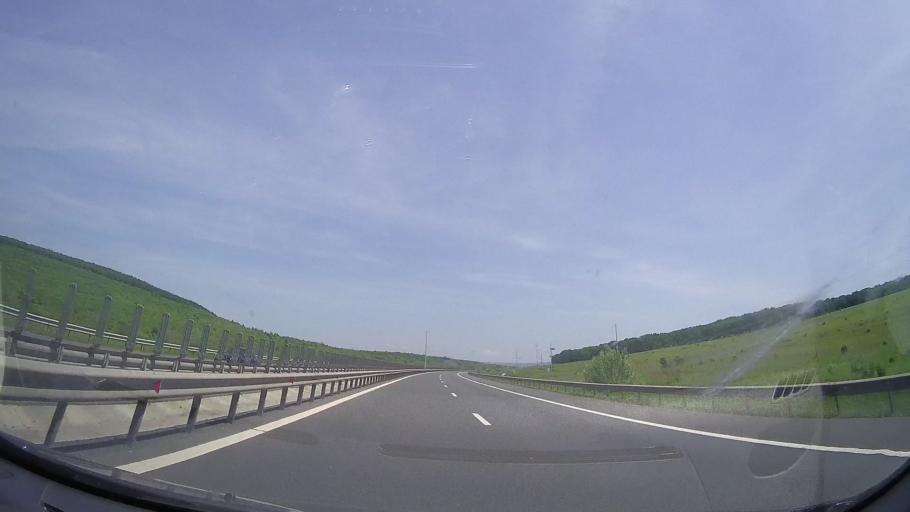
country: RO
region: Sibiu
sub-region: Comuna Cristian
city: Cristian
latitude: 45.7983
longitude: 24.0273
